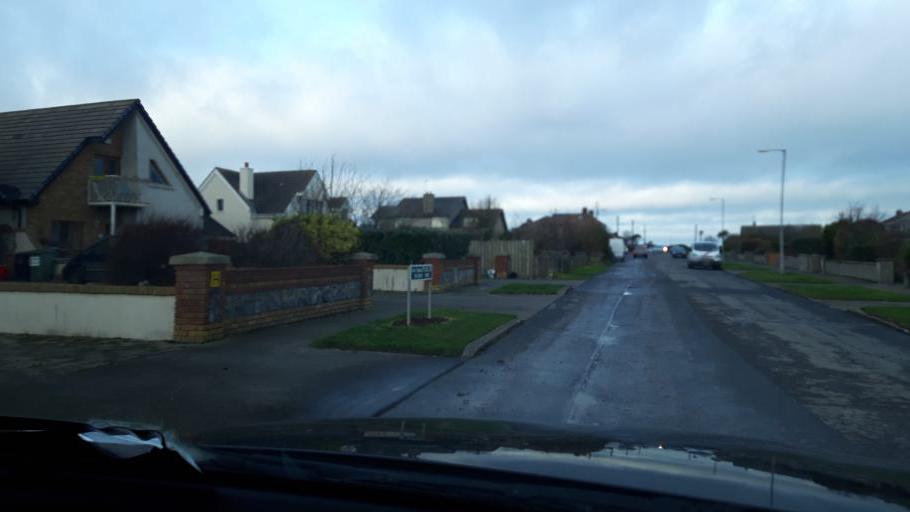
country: IE
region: Leinster
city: An Ros
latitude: 53.5197
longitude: -6.0790
